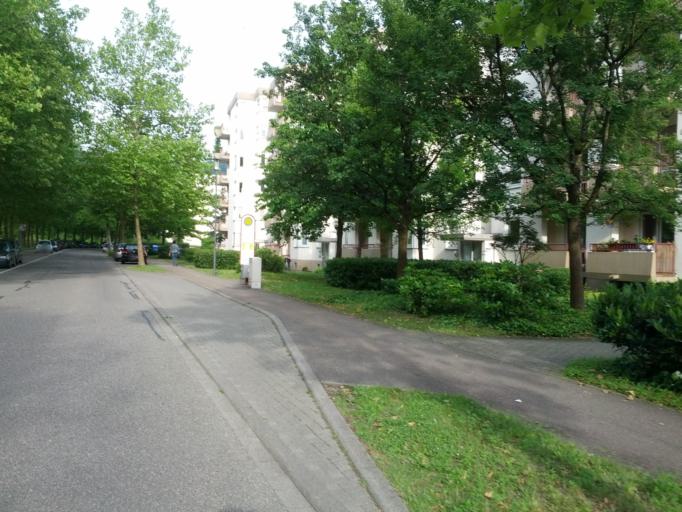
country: DE
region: Baden-Wuerttemberg
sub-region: Freiburg Region
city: Heuweiler
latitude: 48.0729
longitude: 7.9077
